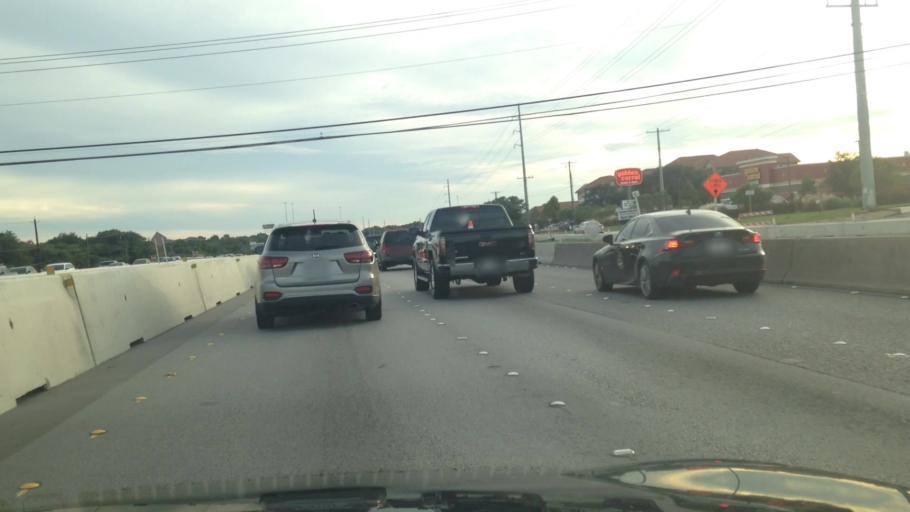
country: US
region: Texas
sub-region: Travis County
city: Onion Creek
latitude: 30.1848
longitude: -97.7745
